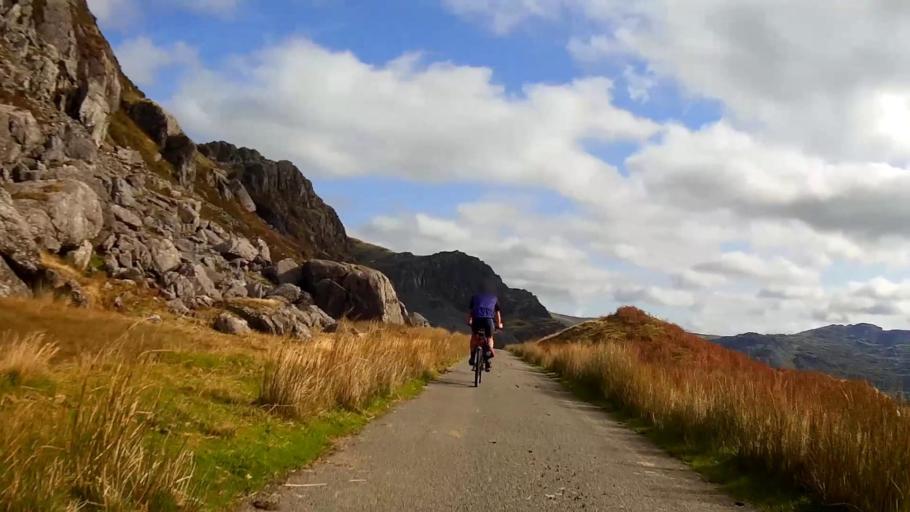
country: GB
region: Wales
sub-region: Gwynedd
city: Maentwrog
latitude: 52.9845
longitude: -3.9762
